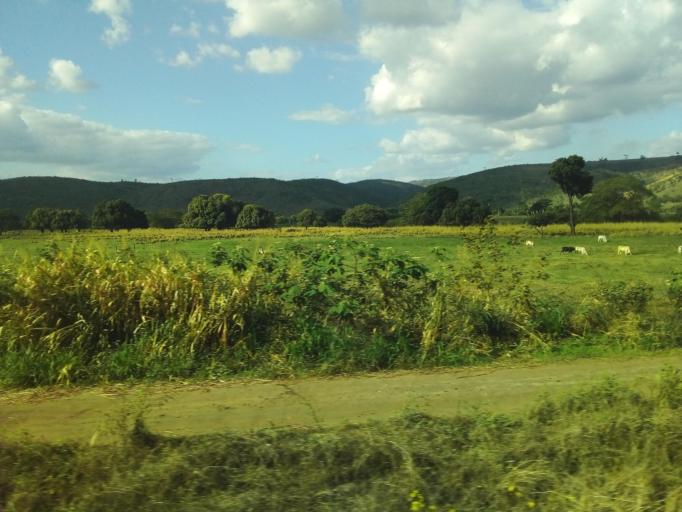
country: BR
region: Minas Gerais
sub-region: Conselheiro Pena
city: Conselheiro Pena
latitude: -19.1208
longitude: -41.5006
